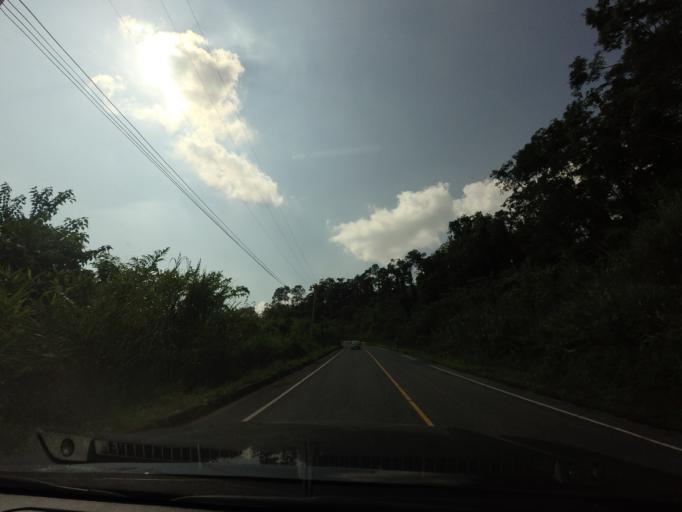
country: TH
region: Nan
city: Santi Suk
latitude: 18.9726
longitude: 100.9790
